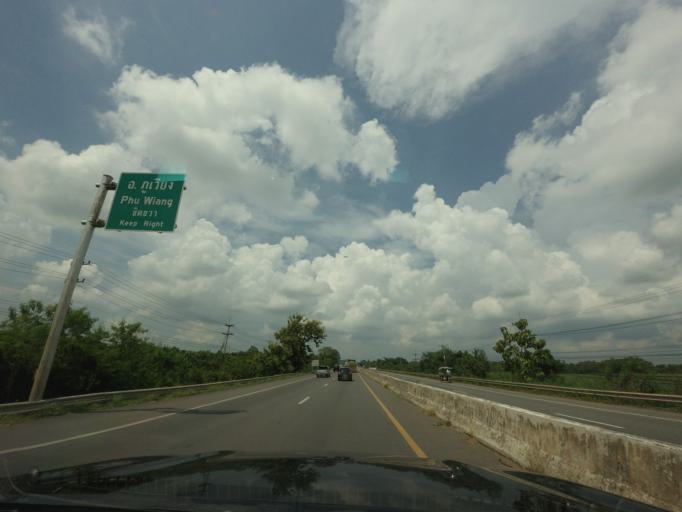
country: TH
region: Khon Kaen
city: Nong Ruea
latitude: 16.4882
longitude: 102.4124
